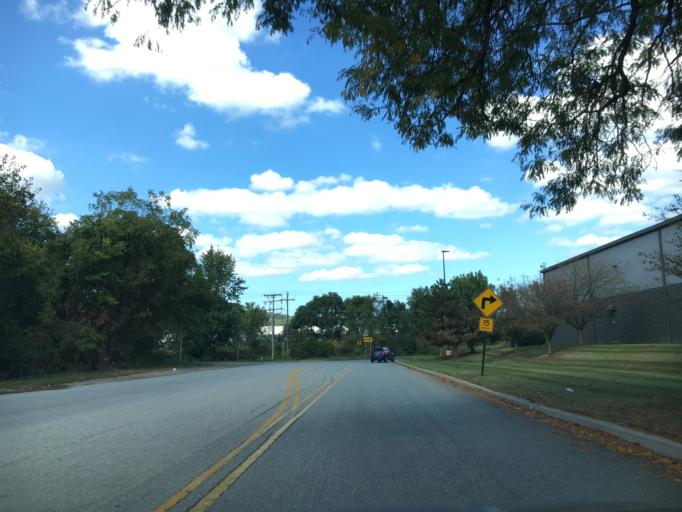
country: US
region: Pennsylvania
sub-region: York County
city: East York
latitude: 39.9803
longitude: -76.6751
